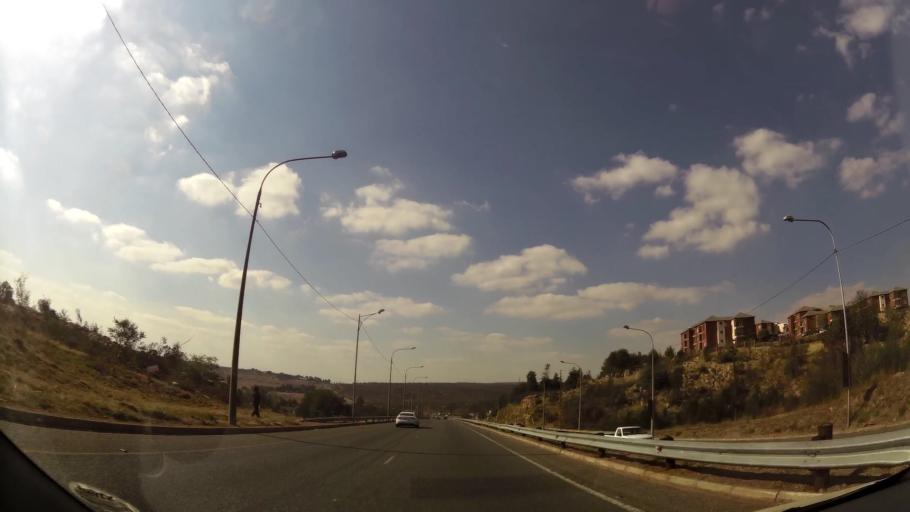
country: ZA
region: Gauteng
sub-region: West Rand District Municipality
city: Krugersdorp
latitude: -26.0755
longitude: 27.7972
